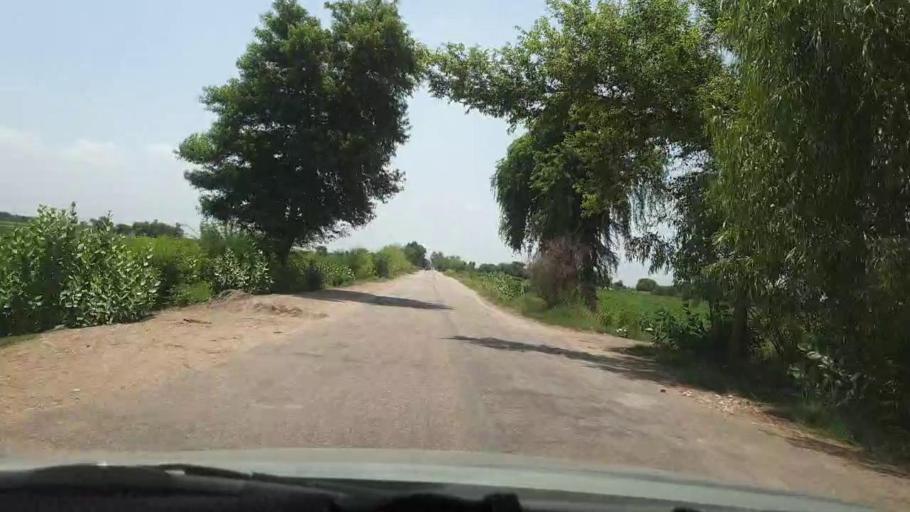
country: PK
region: Sindh
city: Pano Aqil
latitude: 27.6694
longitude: 69.1062
